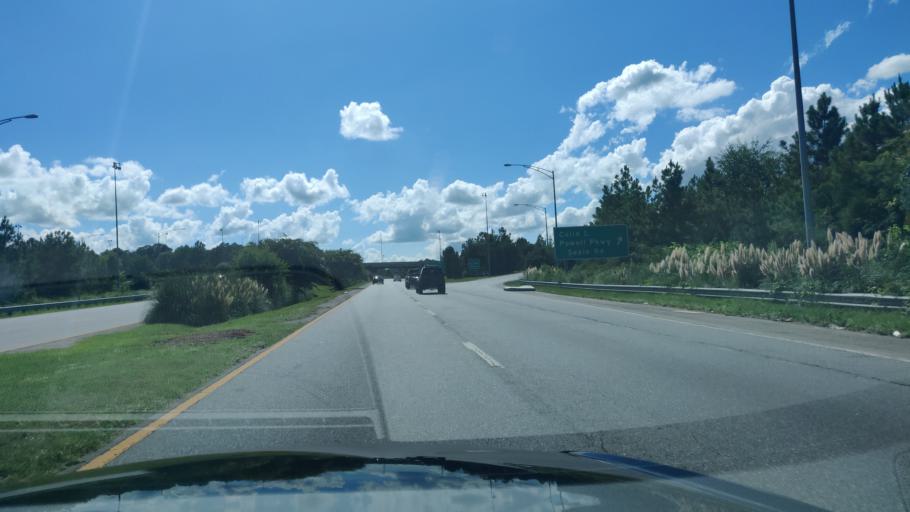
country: US
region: Georgia
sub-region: Muscogee County
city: Columbus
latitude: 32.4530
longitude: -84.9980
